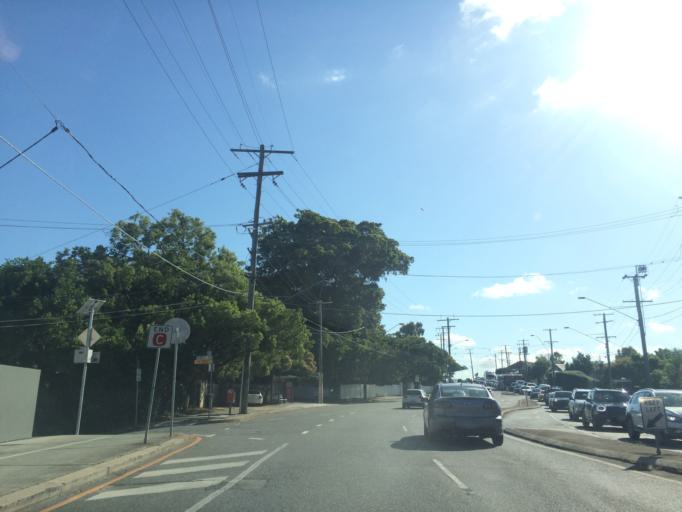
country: AU
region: Queensland
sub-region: Brisbane
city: Balmoral
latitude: -27.4735
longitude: 153.0569
